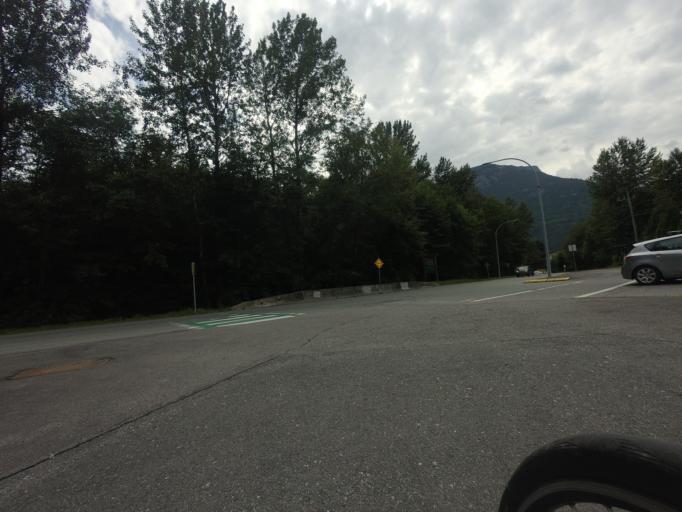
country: CA
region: British Columbia
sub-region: Greater Vancouver Regional District
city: Lions Bay
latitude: 49.7298
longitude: -123.1458
